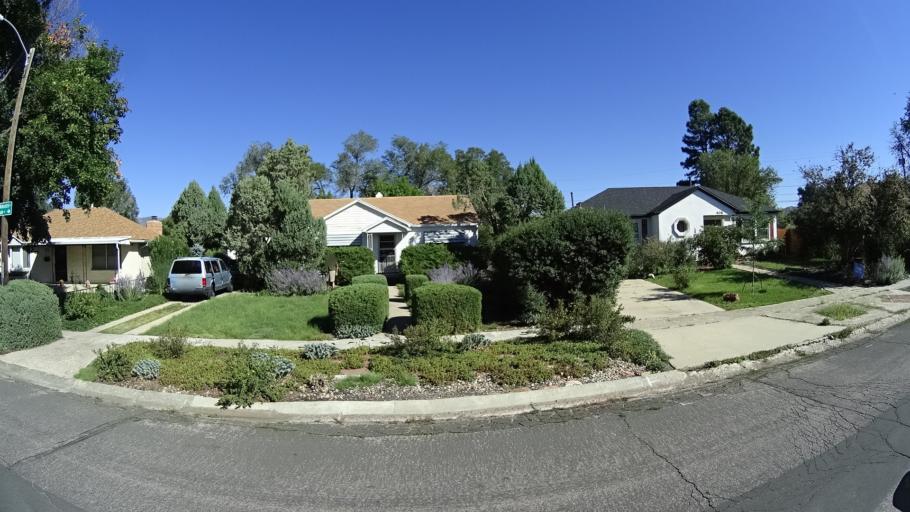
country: US
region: Colorado
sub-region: El Paso County
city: Colorado Springs
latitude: 38.8699
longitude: -104.8166
